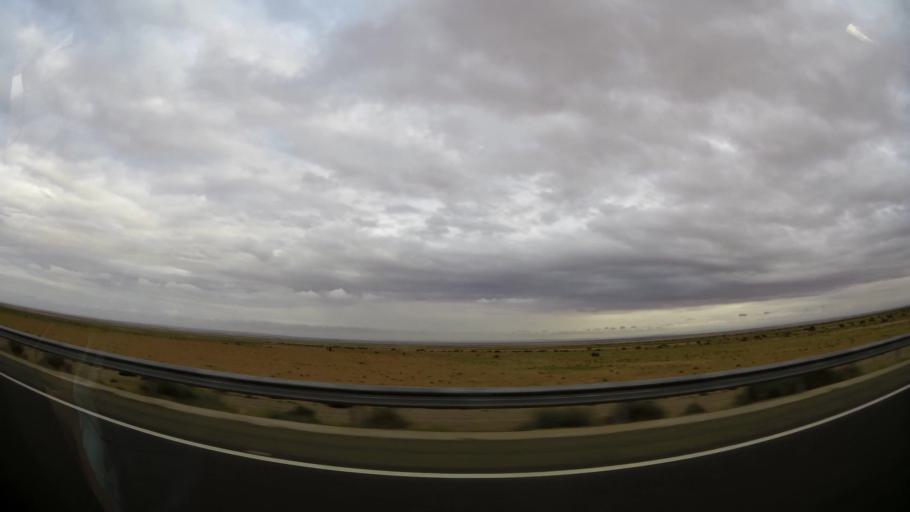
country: MA
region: Taza-Al Hoceima-Taounate
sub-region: Taza
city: Guercif
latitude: 34.3134
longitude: -3.5961
